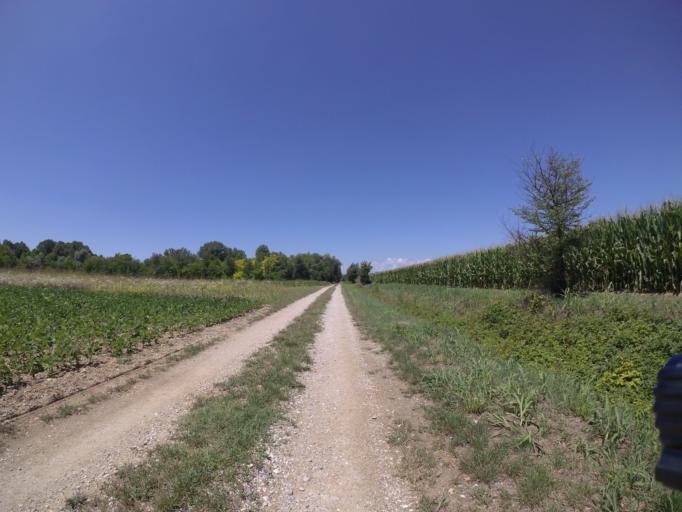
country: IT
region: Friuli Venezia Giulia
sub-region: Provincia di Udine
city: Teor
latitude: 45.8773
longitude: 13.0761
